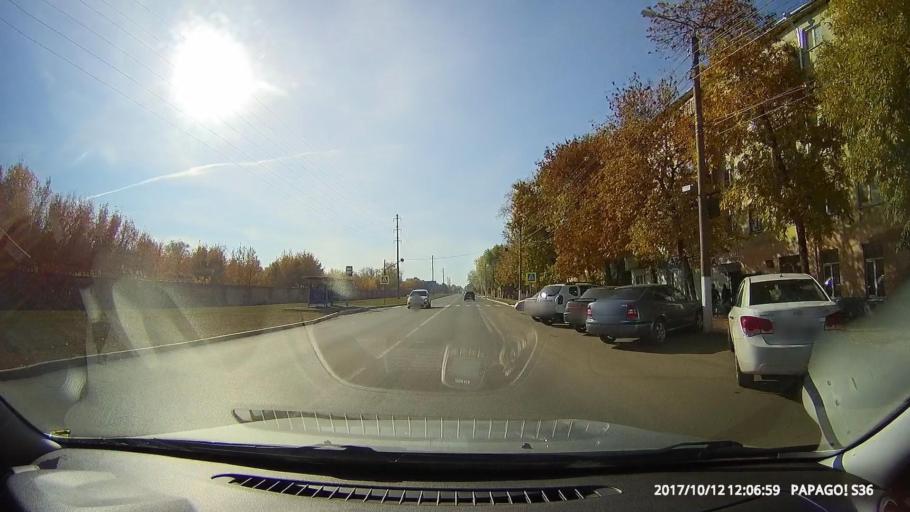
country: RU
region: Samara
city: Chapayevsk
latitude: 52.9697
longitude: 49.7040
